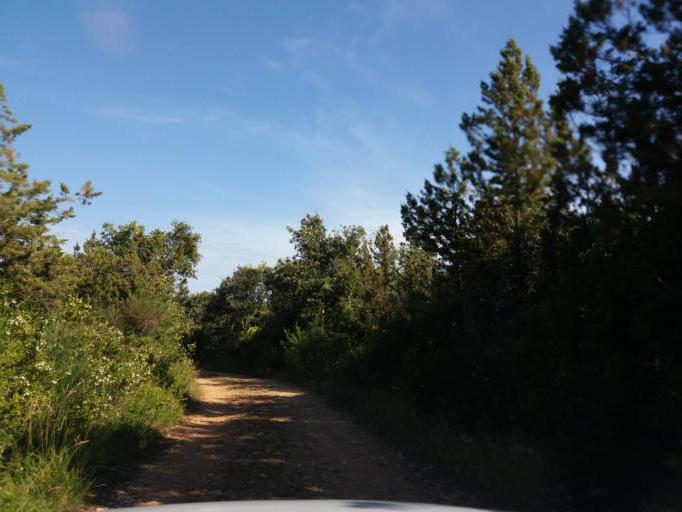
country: HR
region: Zadarska
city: Ugljan
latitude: 44.1316
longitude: 14.8625
